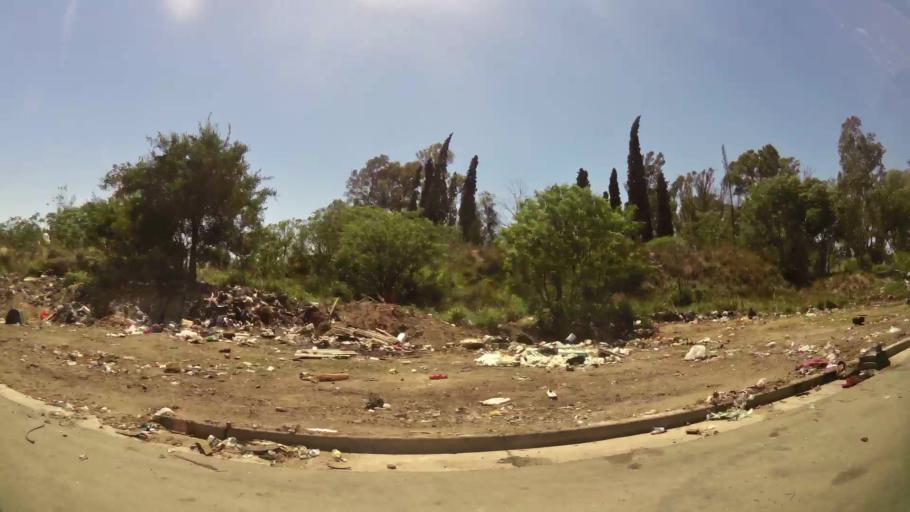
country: AR
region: Cordoba
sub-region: Departamento de Capital
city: Cordoba
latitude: -31.4068
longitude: -64.1347
